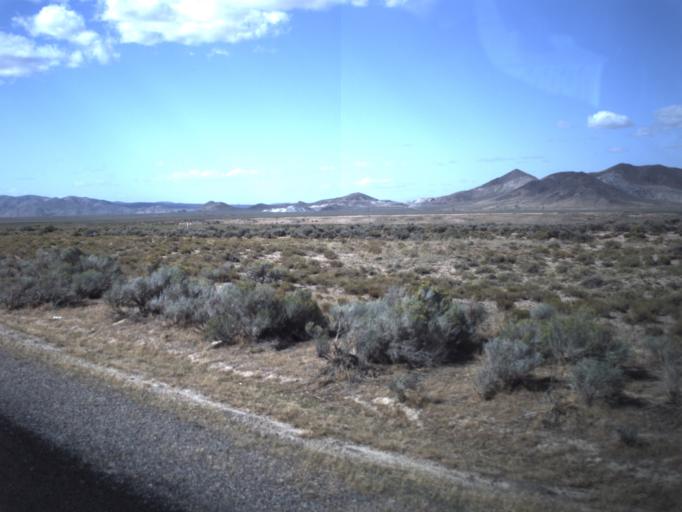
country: US
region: Utah
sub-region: Beaver County
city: Milford
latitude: 38.4623
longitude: -113.0024
